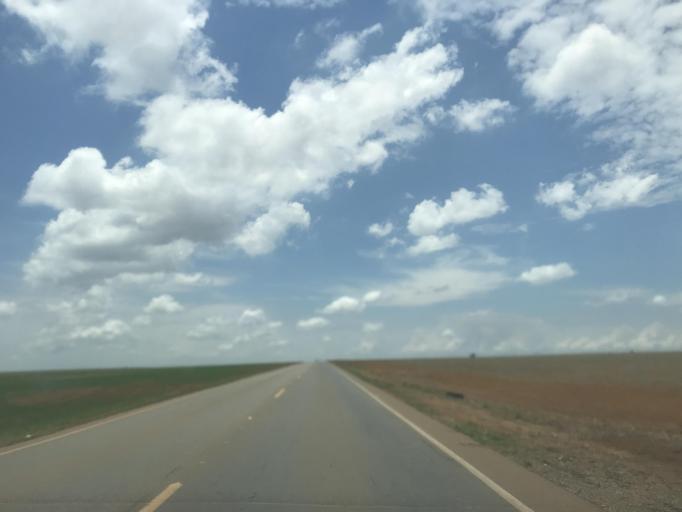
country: BR
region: Goias
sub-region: Vianopolis
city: Vianopolis
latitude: -16.5174
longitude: -48.2360
